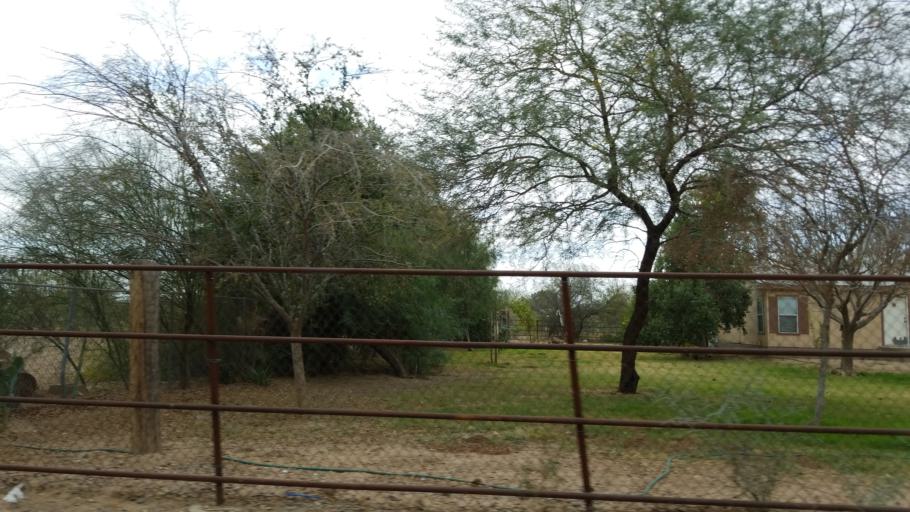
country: US
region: Arizona
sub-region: Maricopa County
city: Laveen
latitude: 33.4097
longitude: -112.1955
